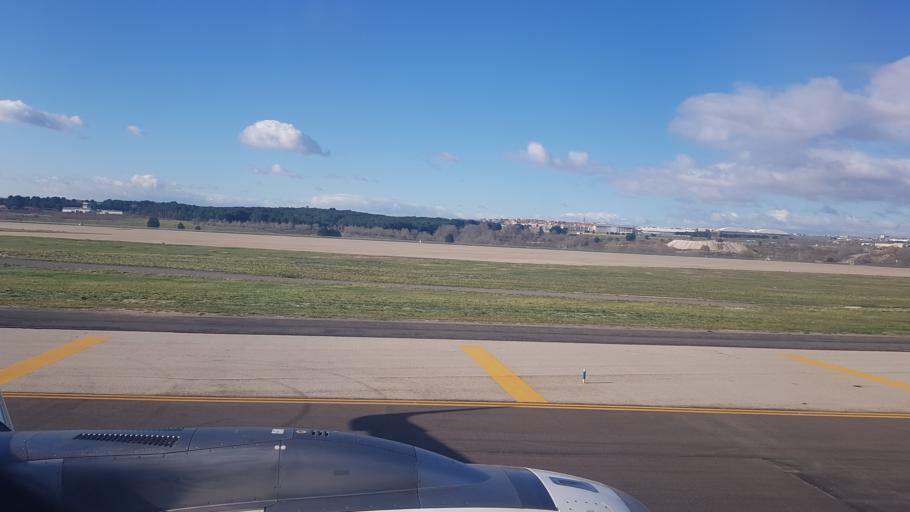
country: ES
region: Madrid
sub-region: Provincia de Madrid
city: Paracuellos de Jarama
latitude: 40.4874
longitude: -3.5504
